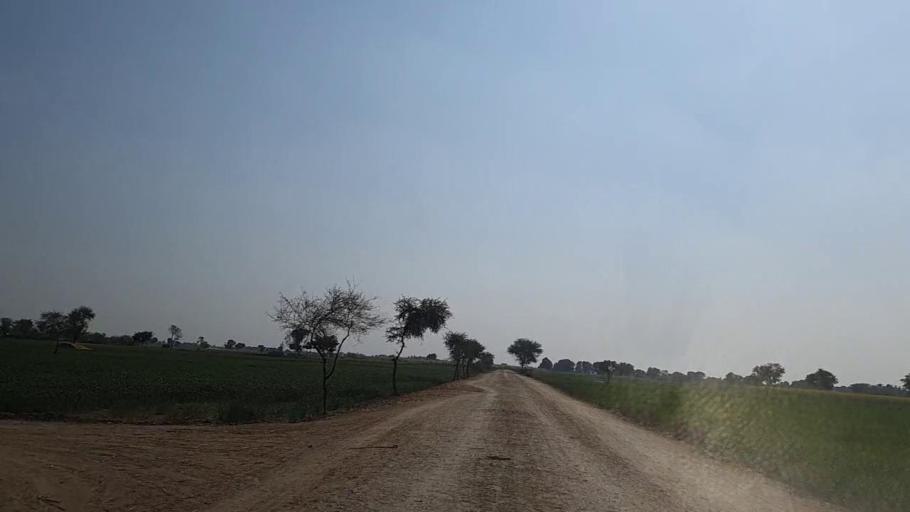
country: PK
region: Sindh
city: Daur
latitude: 26.4733
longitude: 68.2509
